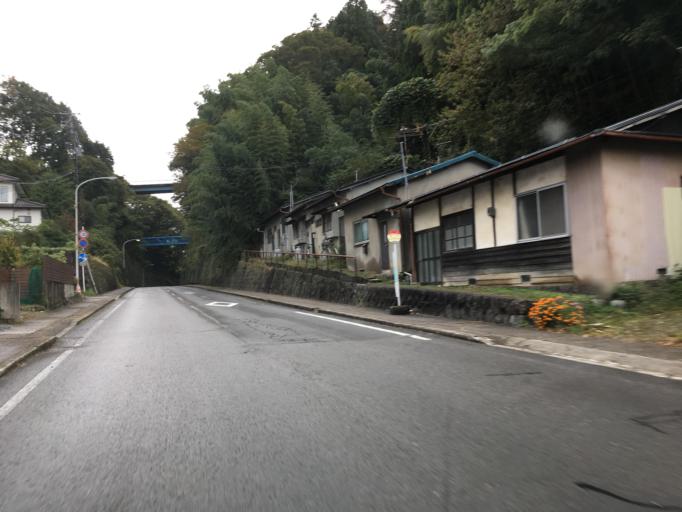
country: JP
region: Fukushima
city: Nihommatsu
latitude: 37.5967
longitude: 140.4400
